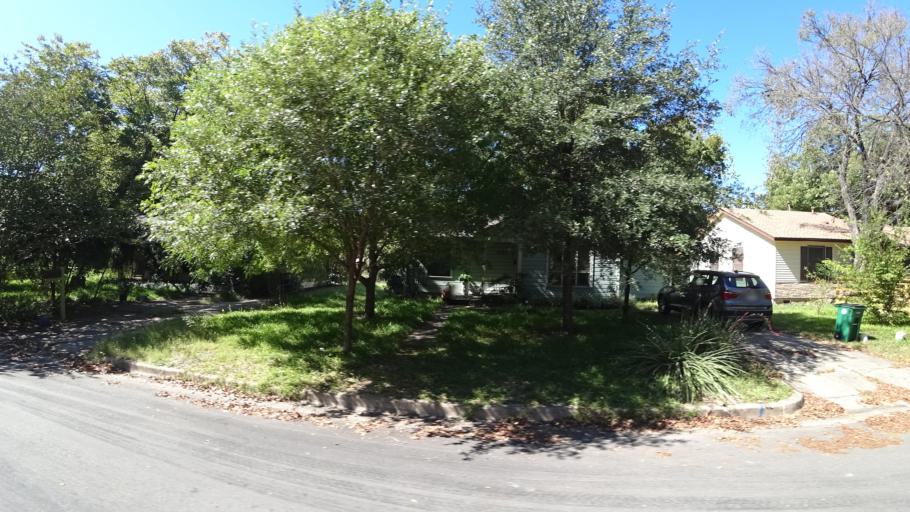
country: US
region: Texas
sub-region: Travis County
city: Austin
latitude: 30.2883
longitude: -97.7101
